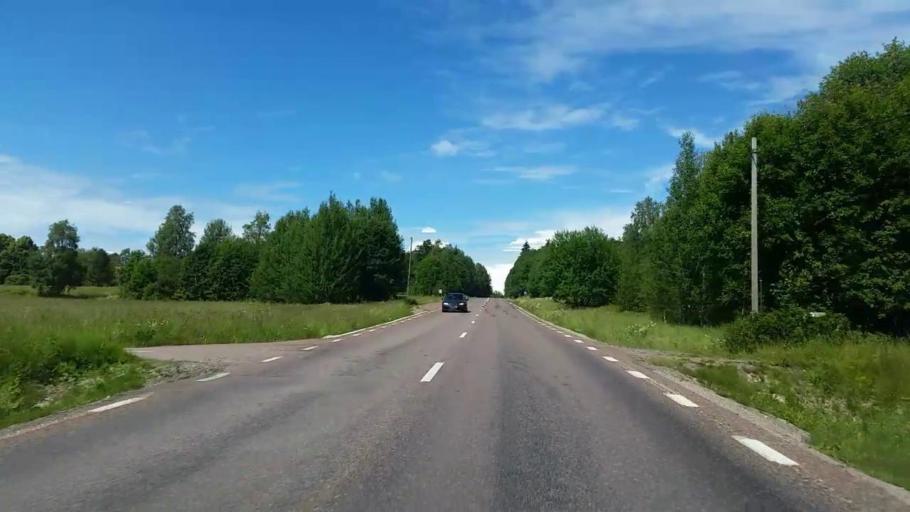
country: SE
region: Dalarna
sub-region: Rattviks Kommun
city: Raettvik
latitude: 61.0137
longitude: 15.2155
